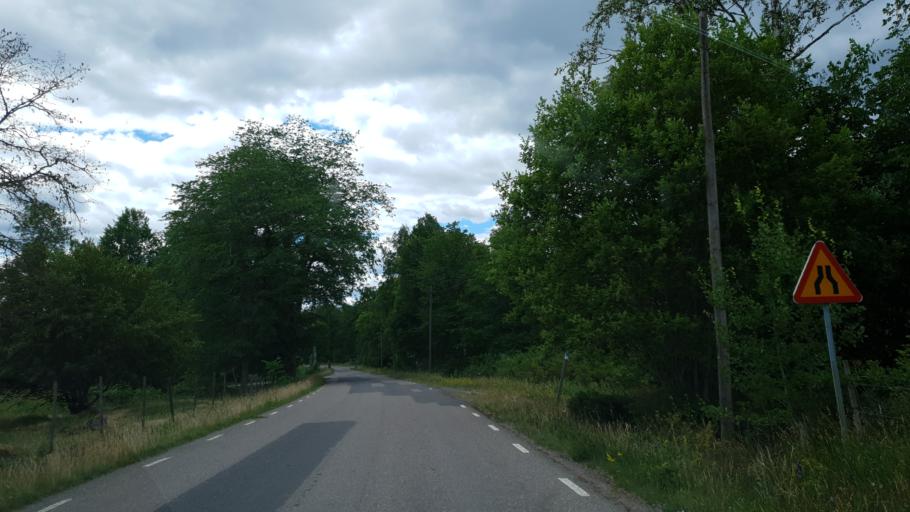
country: SE
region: Kronoberg
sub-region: Uppvidinge Kommun
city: Aseda
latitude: 57.0451
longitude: 15.5803
